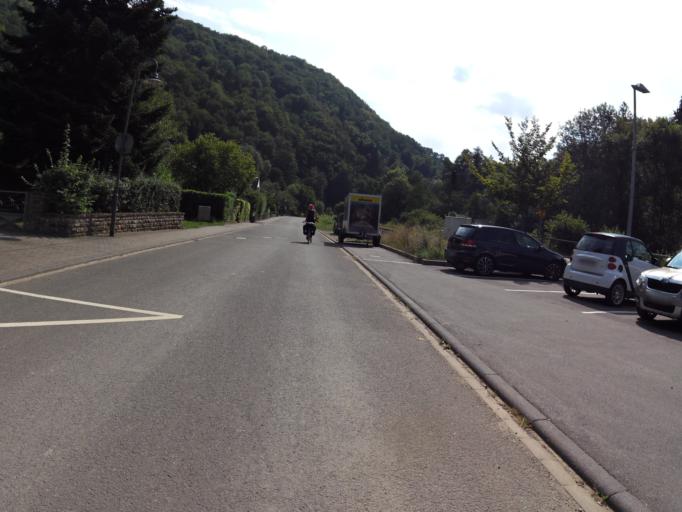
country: DE
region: Rheinland-Pfalz
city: Orenhofen
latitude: 49.8759
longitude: 6.6407
